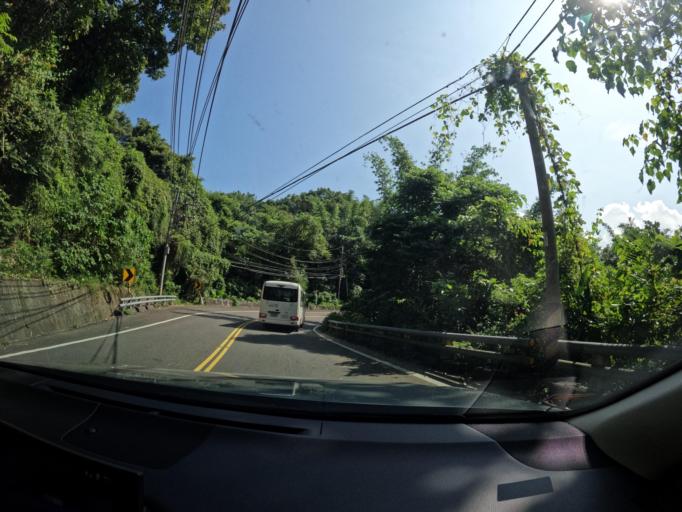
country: TW
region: Taiwan
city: Yujing
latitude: 23.0706
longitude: 120.6548
